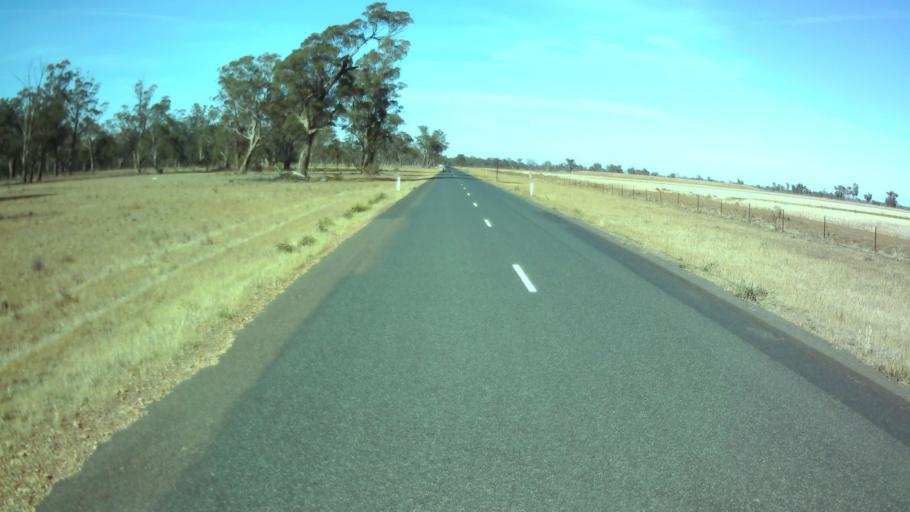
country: AU
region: New South Wales
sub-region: Weddin
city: Grenfell
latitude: -34.1241
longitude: 147.8061
